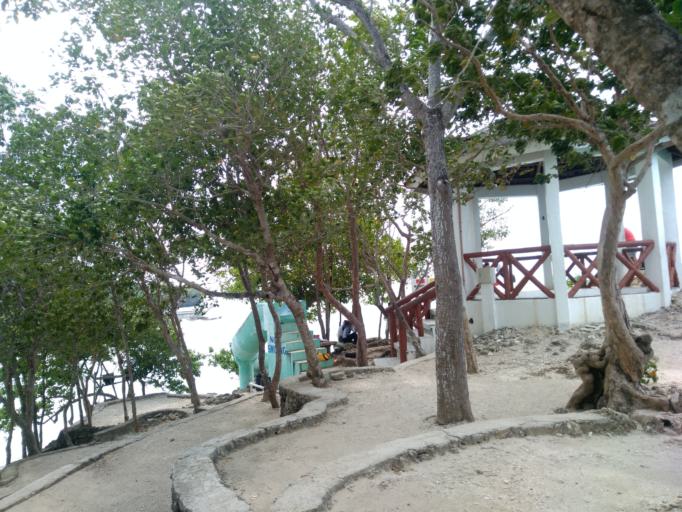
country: PH
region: Central Visayas
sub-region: Province of Siquijor
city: Maria
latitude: 9.2123
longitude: 123.6810
